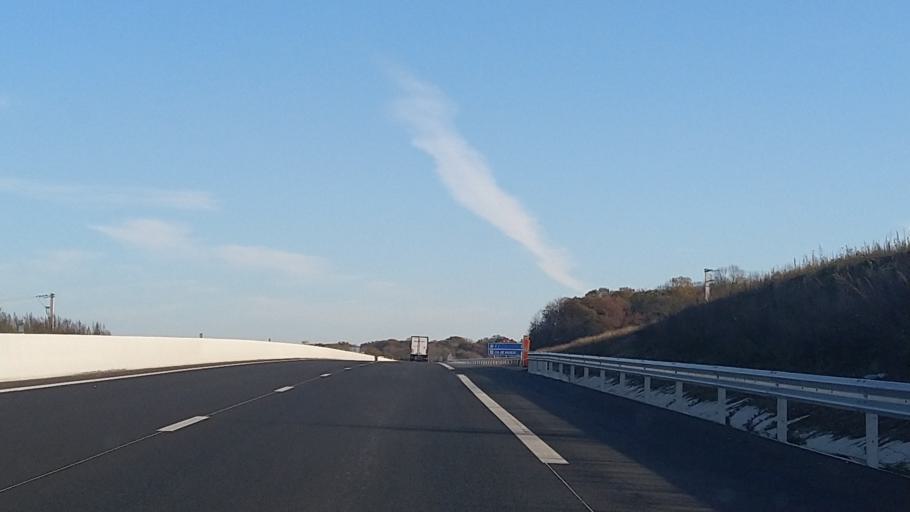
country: FR
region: Ile-de-France
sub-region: Departement du Val-d'Oise
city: Maffliers
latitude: 49.0988
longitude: 2.2860
